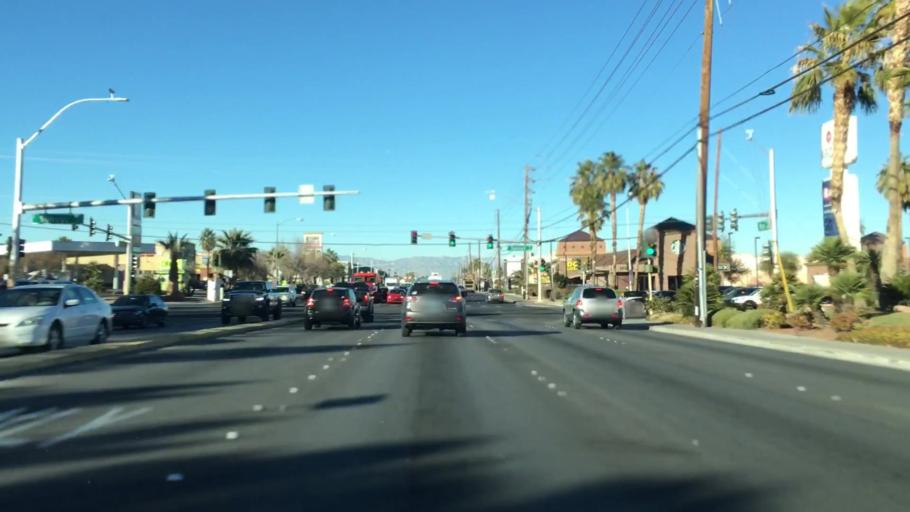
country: US
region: Nevada
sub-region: Clark County
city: Whitney
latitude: 36.0710
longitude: -115.1008
